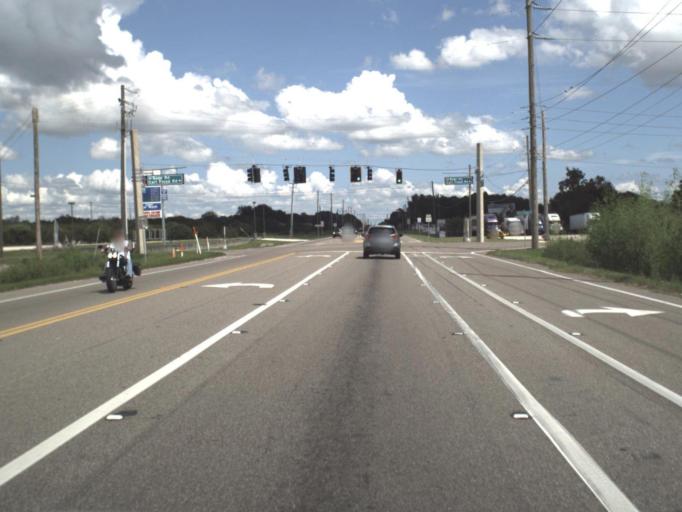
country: US
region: Florida
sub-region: Polk County
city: Cypress Gardens
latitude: 28.0224
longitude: -81.6783
